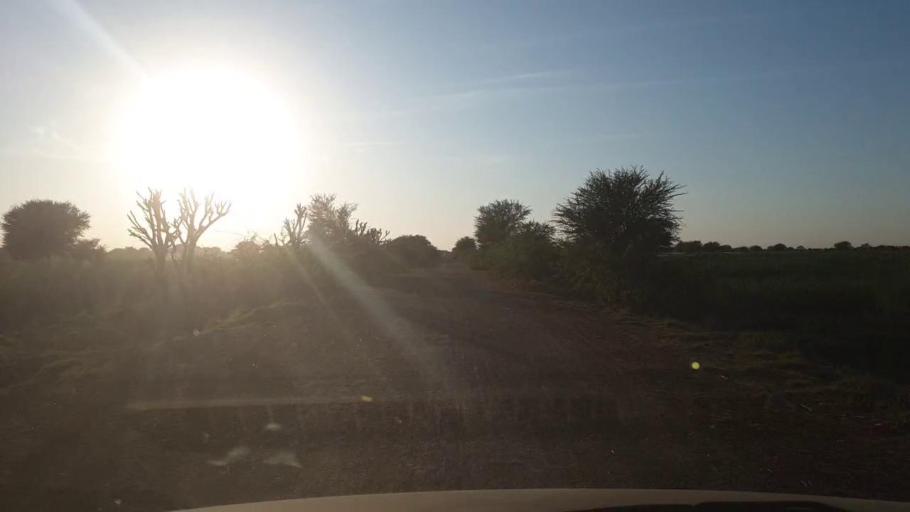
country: PK
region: Sindh
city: Dhoro Naro
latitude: 25.3634
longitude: 69.5695
